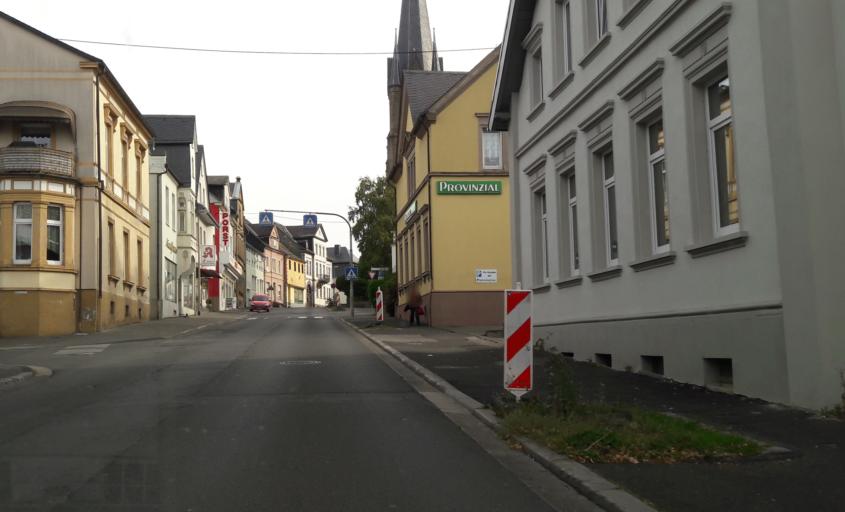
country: DE
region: Rheinland-Pfalz
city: Birkenfeld
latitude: 49.6486
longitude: 7.1662
